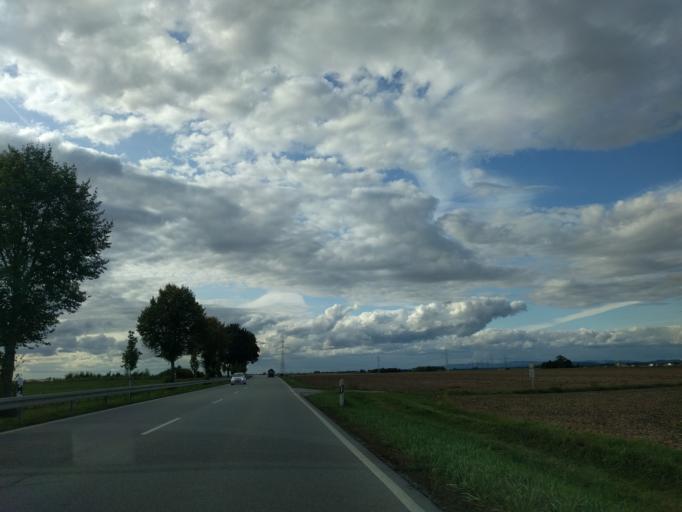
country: DE
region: Bavaria
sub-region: Lower Bavaria
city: Stephansposching
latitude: 48.8100
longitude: 12.7758
